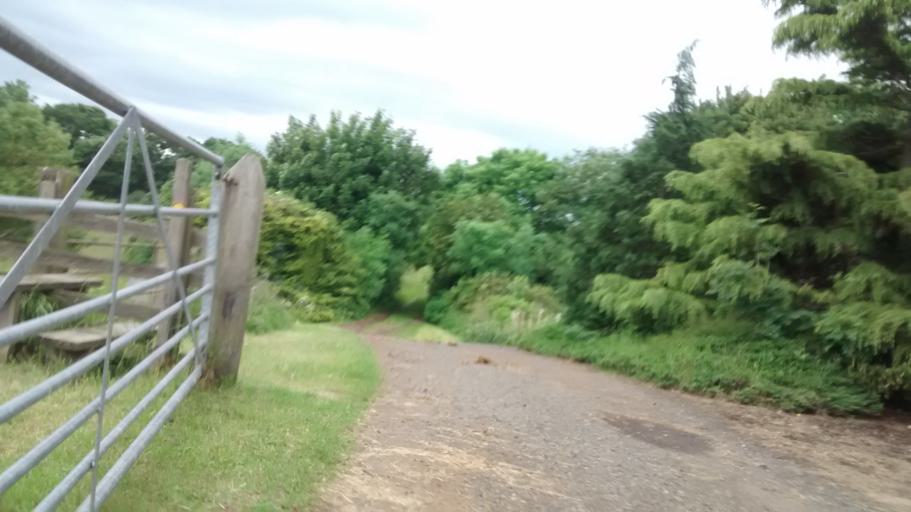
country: GB
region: England
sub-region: County Durham
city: Durham
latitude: 54.7920
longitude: -1.5632
